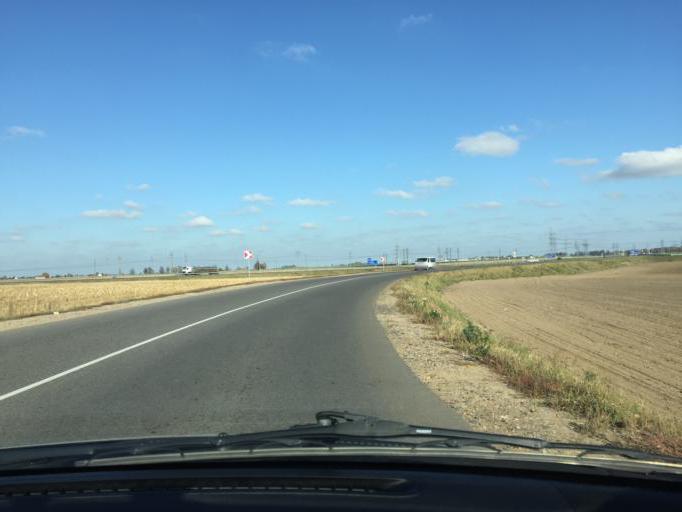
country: BY
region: Minsk
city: Slutsk
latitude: 53.0480
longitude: 27.5276
